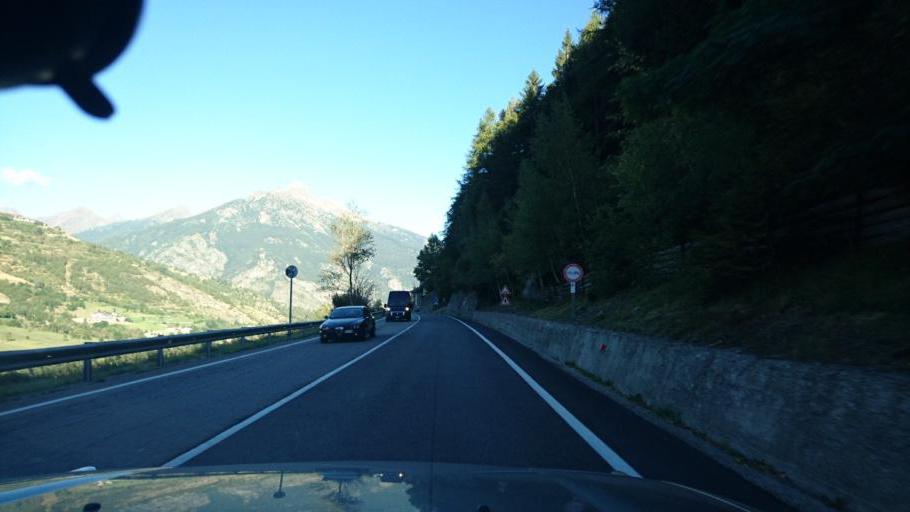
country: IT
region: Aosta Valley
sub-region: Valle d'Aosta
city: Allein
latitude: 45.8037
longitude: 7.2597
